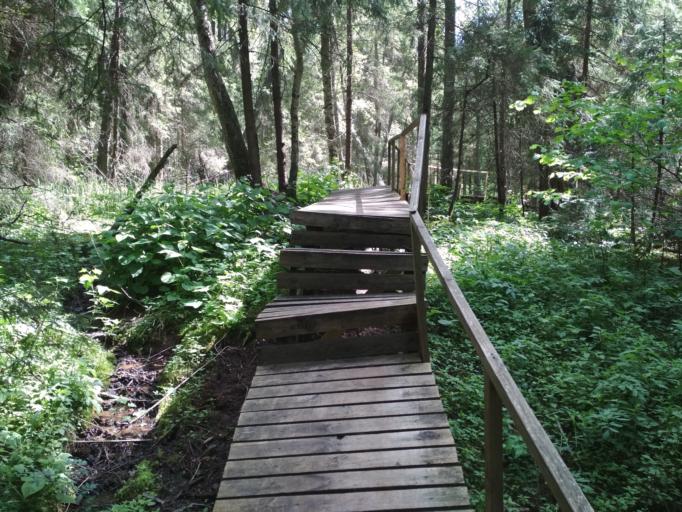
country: BY
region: Minsk
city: Radashkovichy
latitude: 54.2014
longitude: 27.3833
